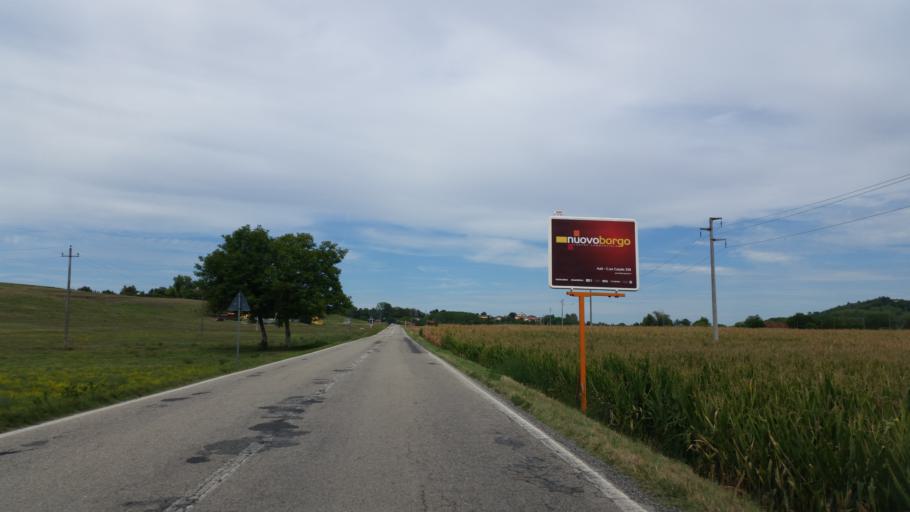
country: IT
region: Piedmont
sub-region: Provincia di Asti
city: Celle Enomondo
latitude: 44.8820
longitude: 8.1332
